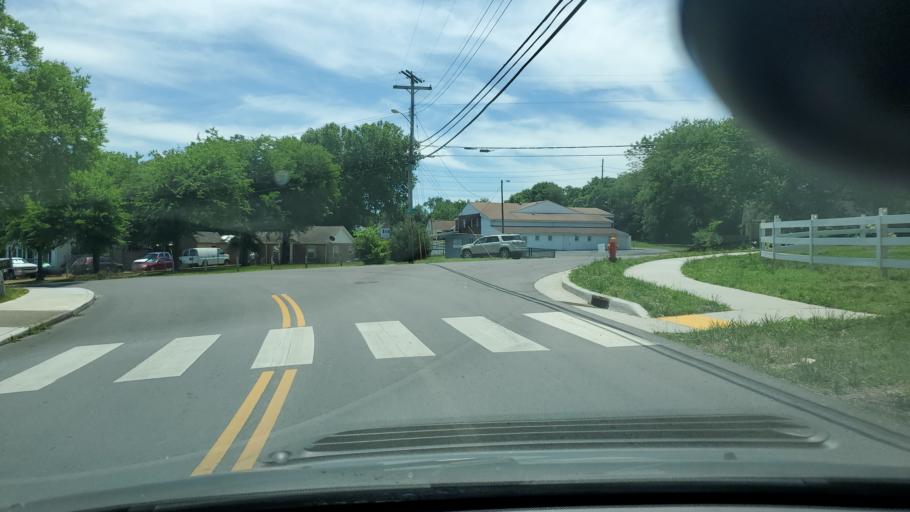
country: US
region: Tennessee
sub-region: Davidson County
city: Nashville
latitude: 36.2068
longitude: -86.7579
